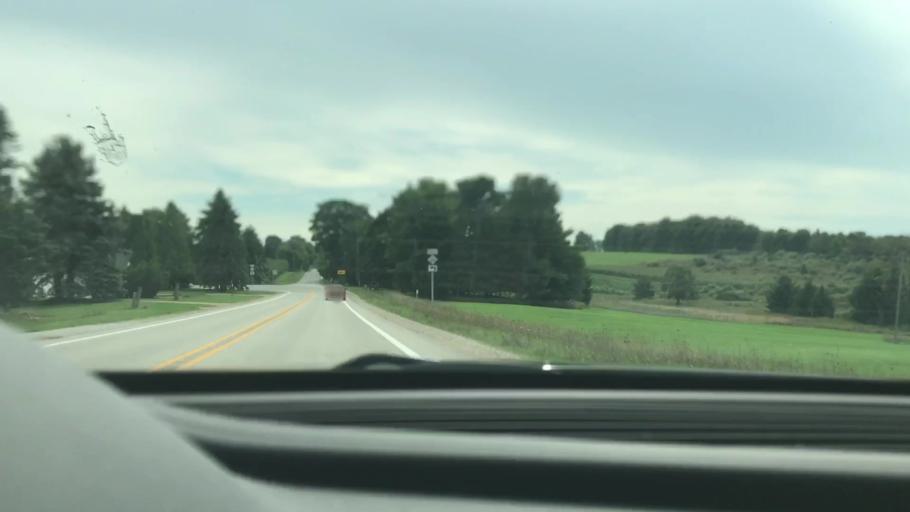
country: US
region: Michigan
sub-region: Antrim County
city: Bellaire
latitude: 45.1003
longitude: -85.3052
